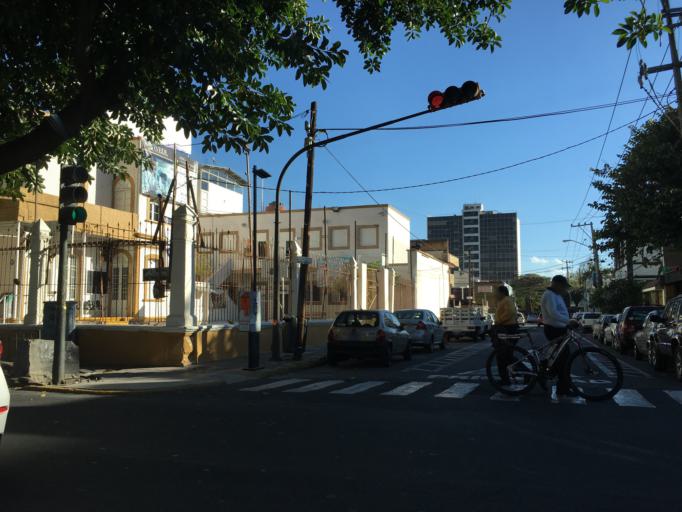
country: MX
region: Jalisco
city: Guadalajara
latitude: 20.6769
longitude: -103.3673
